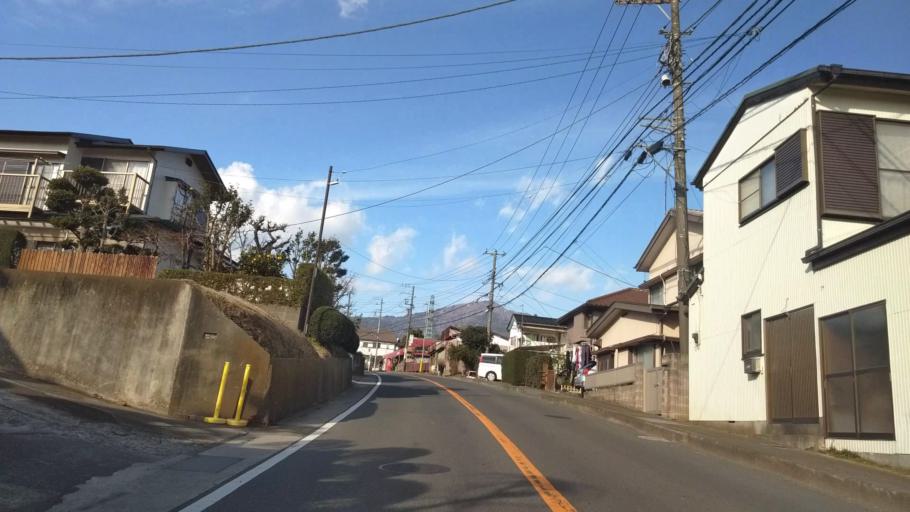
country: JP
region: Kanagawa
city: Hadano
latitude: 35.3844
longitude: 139.2377
